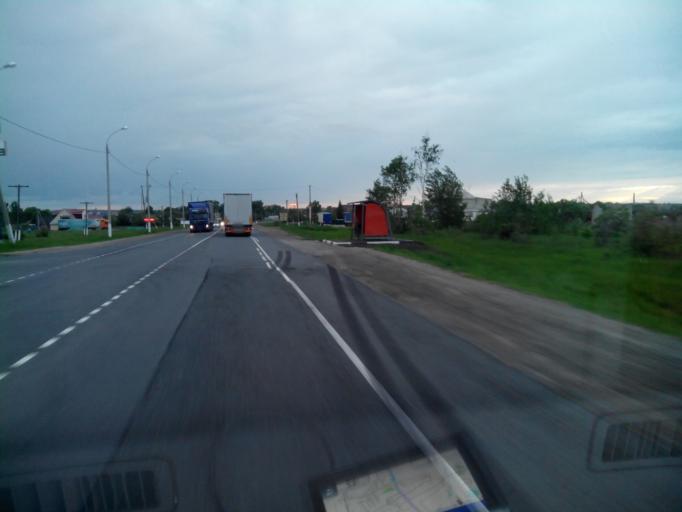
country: RU
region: Penza
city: Chemodanovka
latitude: 53.2188
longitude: 45.3065
